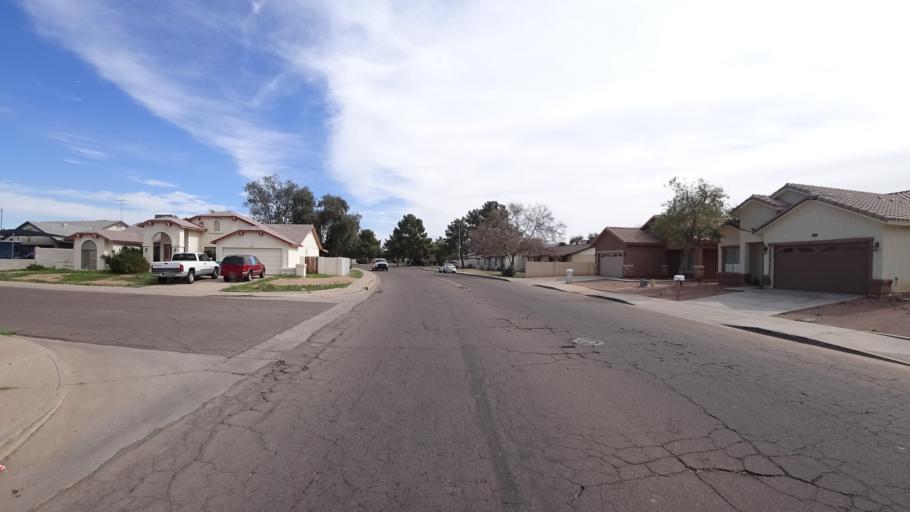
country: US
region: Arizona
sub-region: Maricopa County
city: Glendale
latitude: 33.4869
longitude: -112.2061
